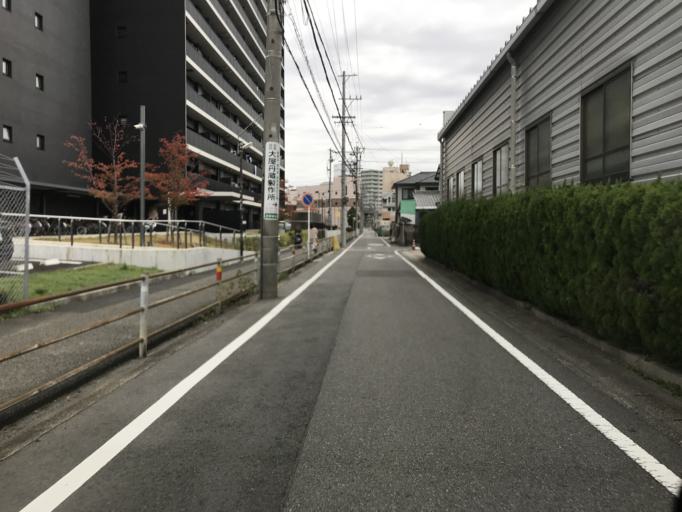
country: JP
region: Aichi
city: Nagoya-shi
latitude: 35.1962
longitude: 136.8600
